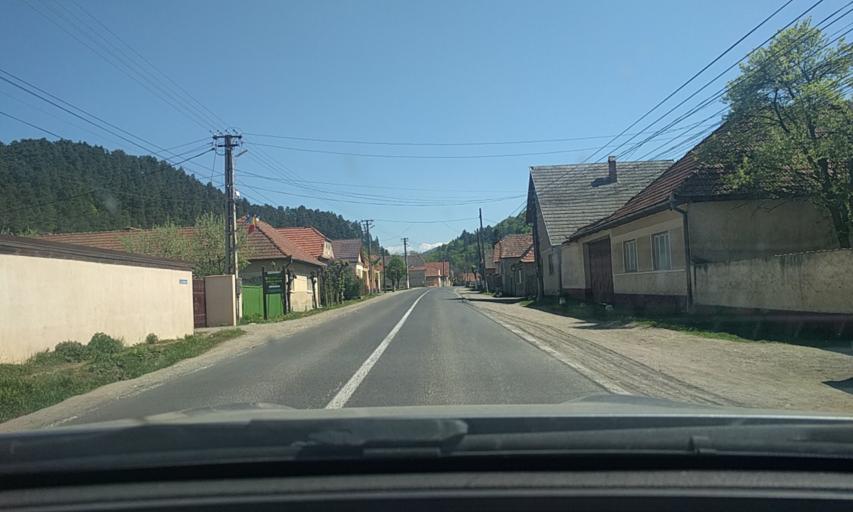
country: RO
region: Brasov
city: Tunelu-Teliu
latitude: 45.7004
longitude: 25.8529
